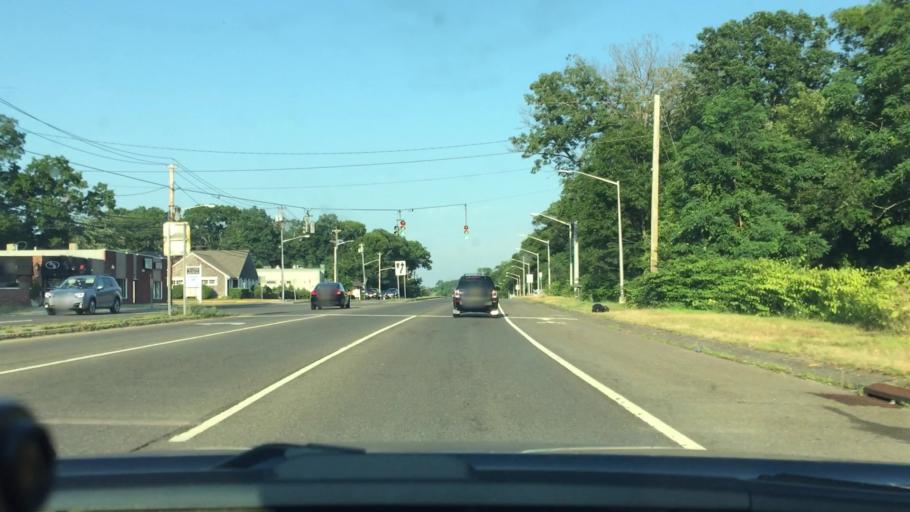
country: US
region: New York
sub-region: Suffolk County
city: Sound Beach
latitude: 40.9451
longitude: -72.9562
